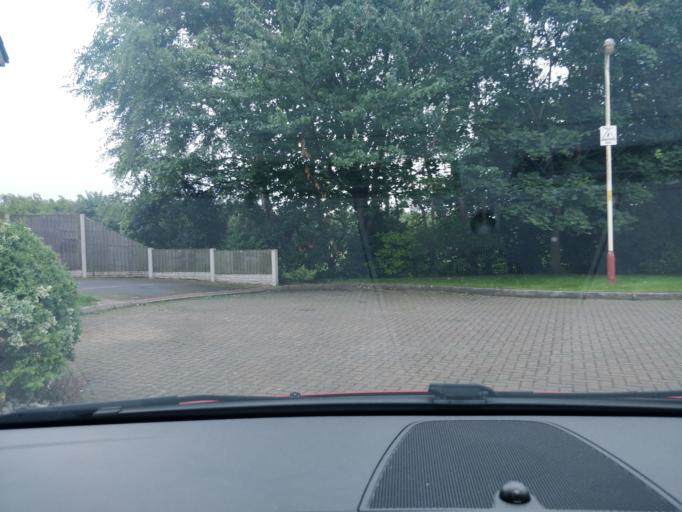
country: GB
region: England
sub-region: Sefton
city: Southport
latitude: 53.6328
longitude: -2.9884
